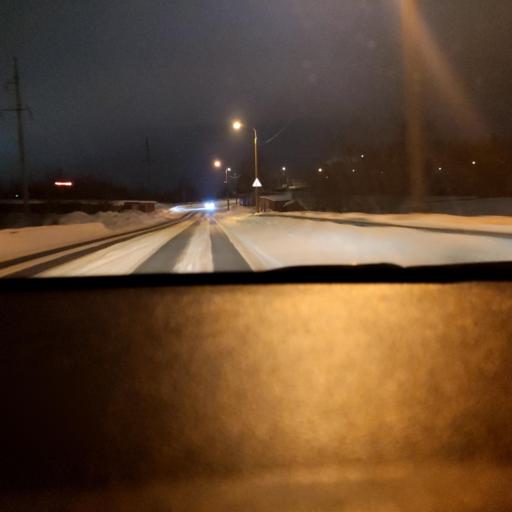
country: RU
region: Tatarstan
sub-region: Chistopol'skiy Rayon
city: Chistopol'
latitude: 55.3595
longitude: 50.6130
